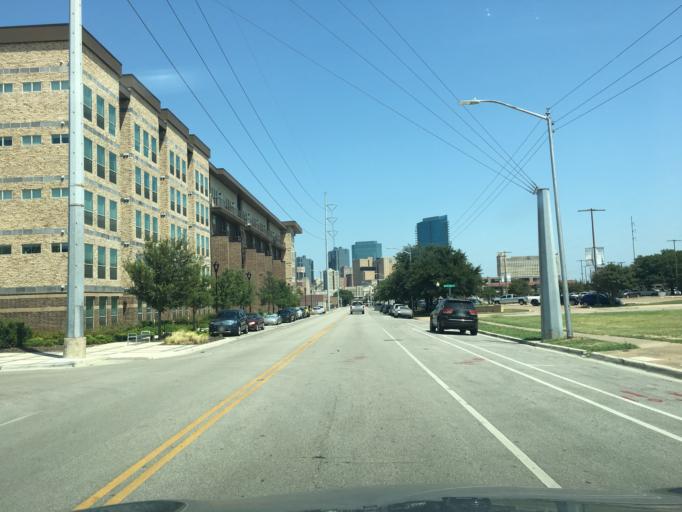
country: US
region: Texas
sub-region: Tarrant County
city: Fort Worth
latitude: 32.7393
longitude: -97.3300
